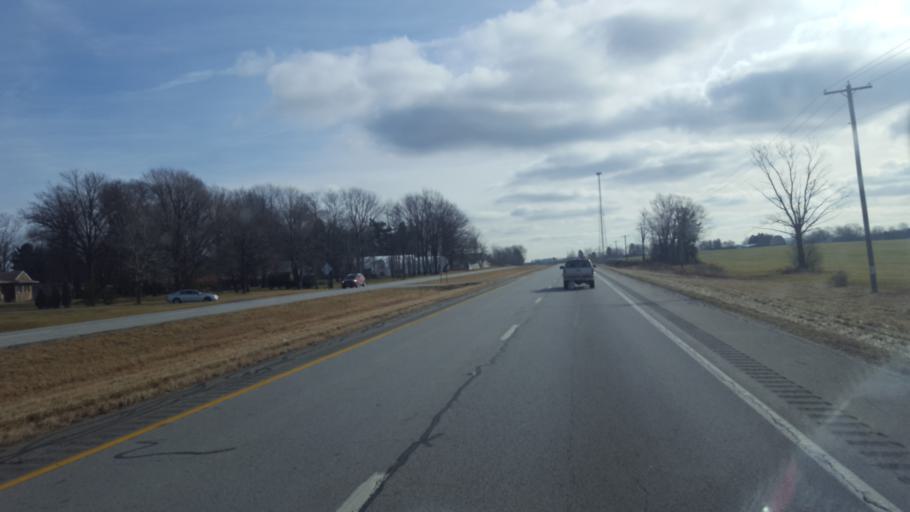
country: US
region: Ohio
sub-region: Wayne County
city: Dalton
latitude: 40.7989
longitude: -81.7139
